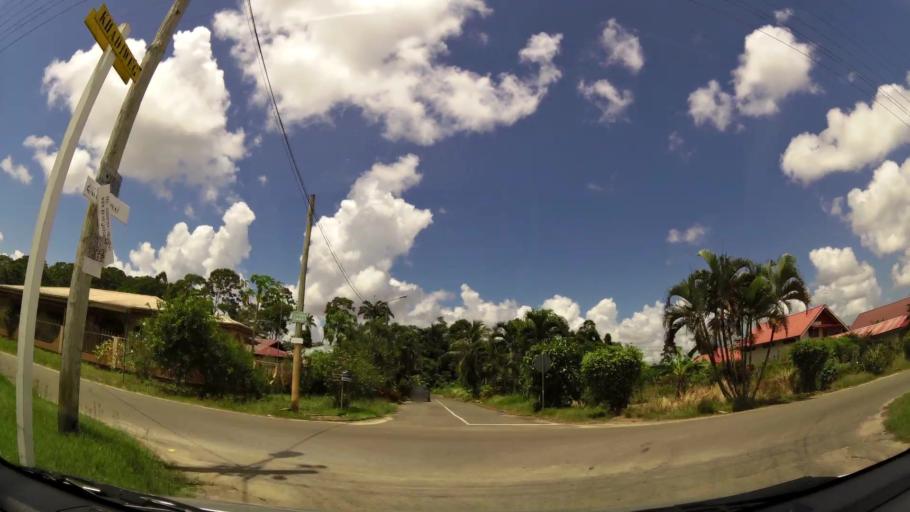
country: SR
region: Paramaribo
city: Paramaribo
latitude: 5.8600
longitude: -55.1648
